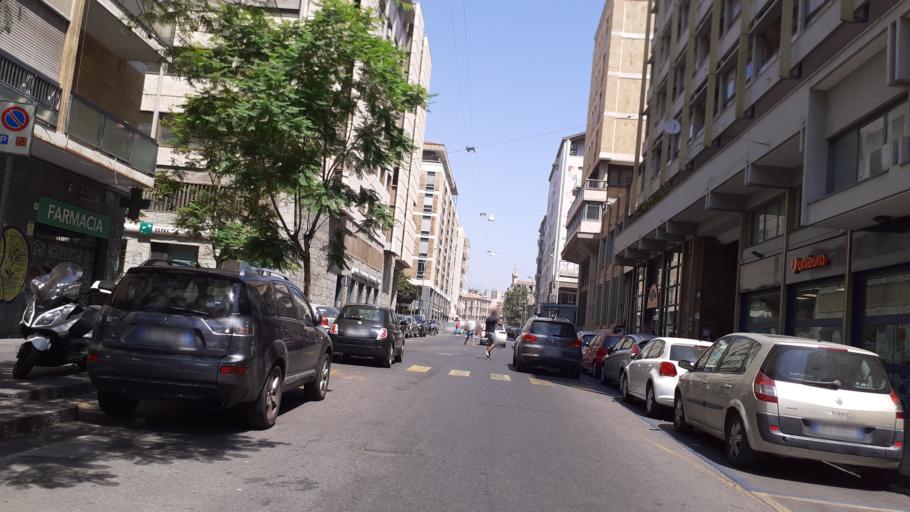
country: IT
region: Sicily
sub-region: Catania
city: Catania
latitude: 37.5067
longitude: 15.0888
